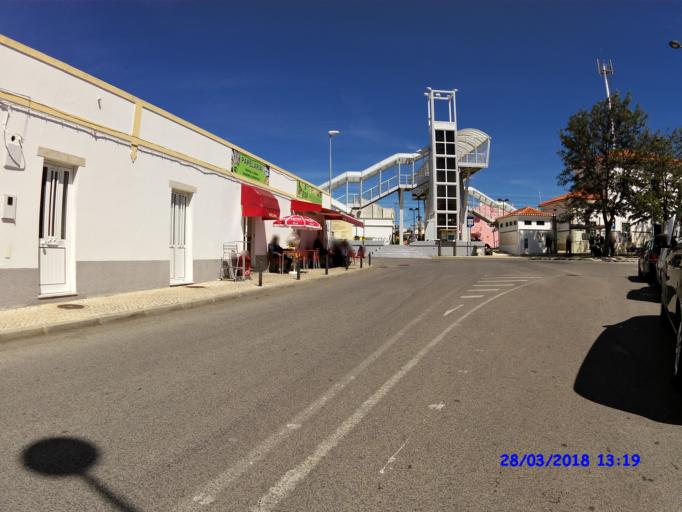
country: PT
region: Faro
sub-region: Albufeira
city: Ferreiras
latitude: 37.1284
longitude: -8.2335
